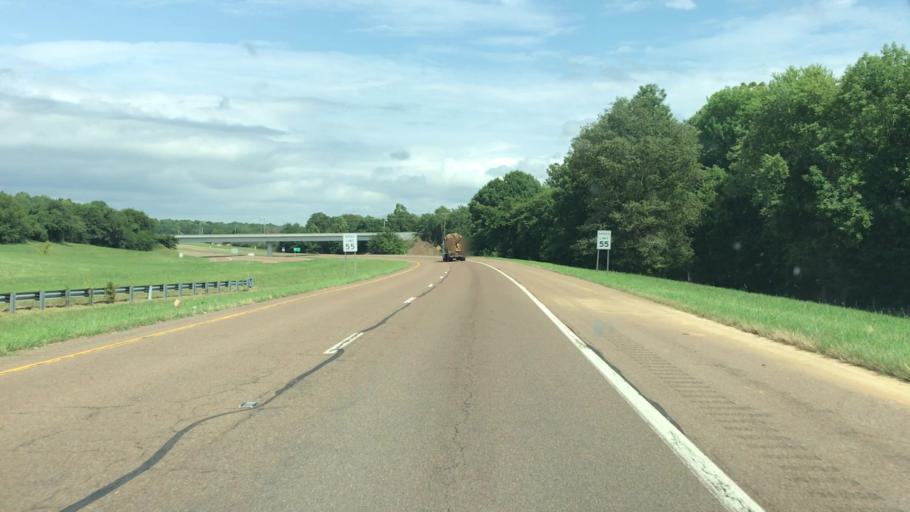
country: US
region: Tennessee
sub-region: Obion County
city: South Fulton
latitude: 36.4949
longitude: -88.9088
